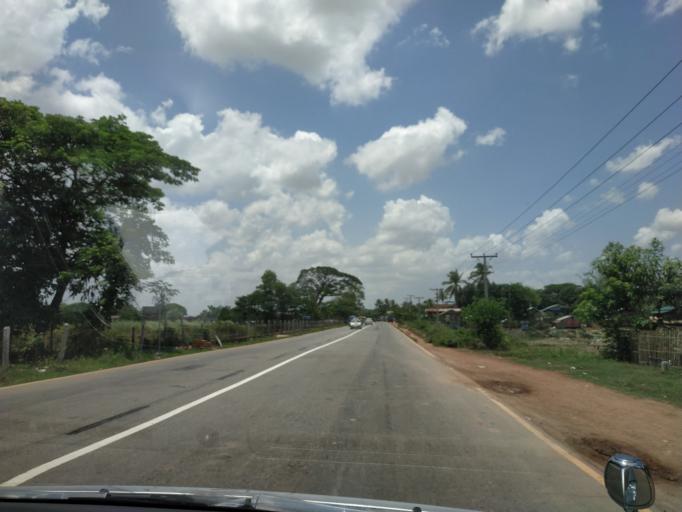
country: MM
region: Bago
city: Thanatpin
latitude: 17.5091
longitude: 96.7147
